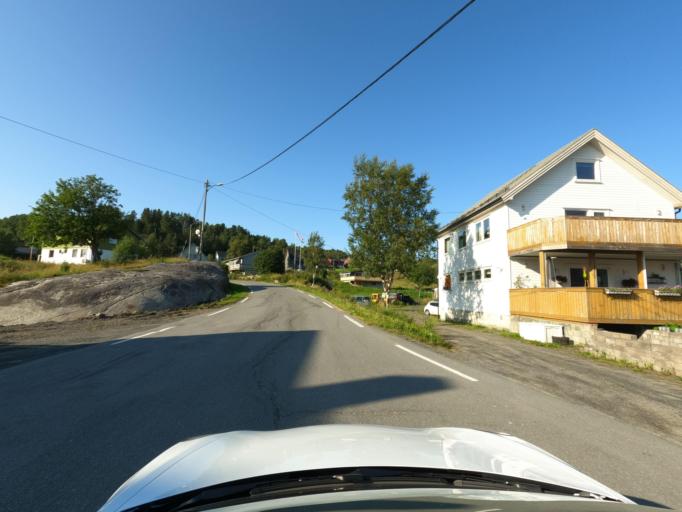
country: NO
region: Nordland
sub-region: Narvik
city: Narvik
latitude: 68.4703
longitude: 17.5042
